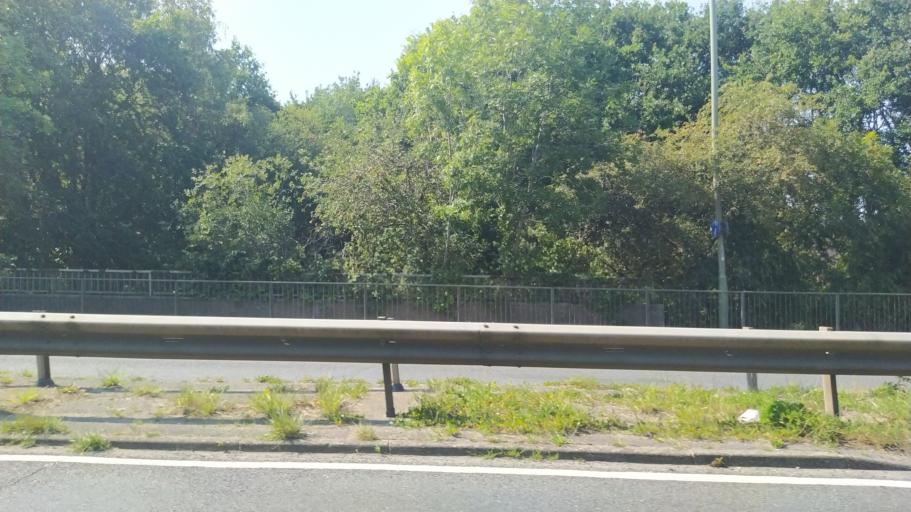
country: GB
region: England
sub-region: Hampshire
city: Totton
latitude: 50.9085
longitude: -1.4962
